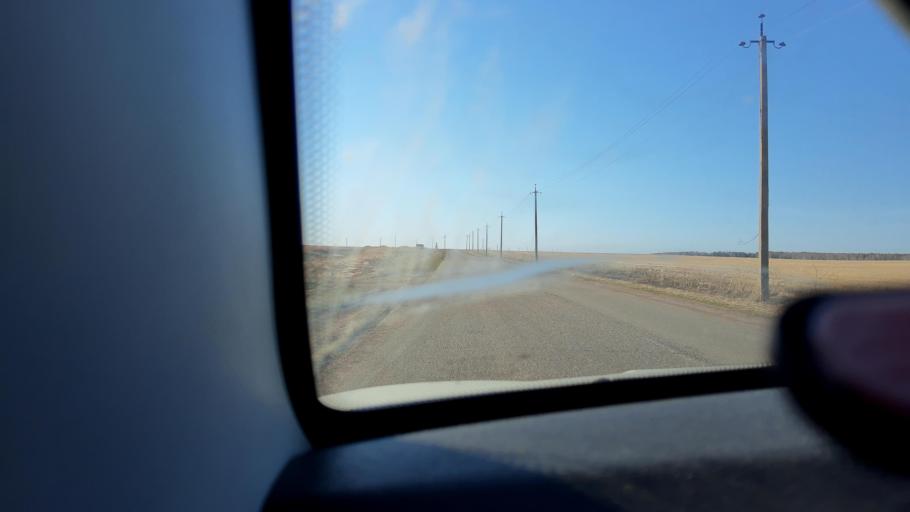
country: RU
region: Bashkortostan
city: Asanovo
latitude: 54.8043
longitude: 55.4897
